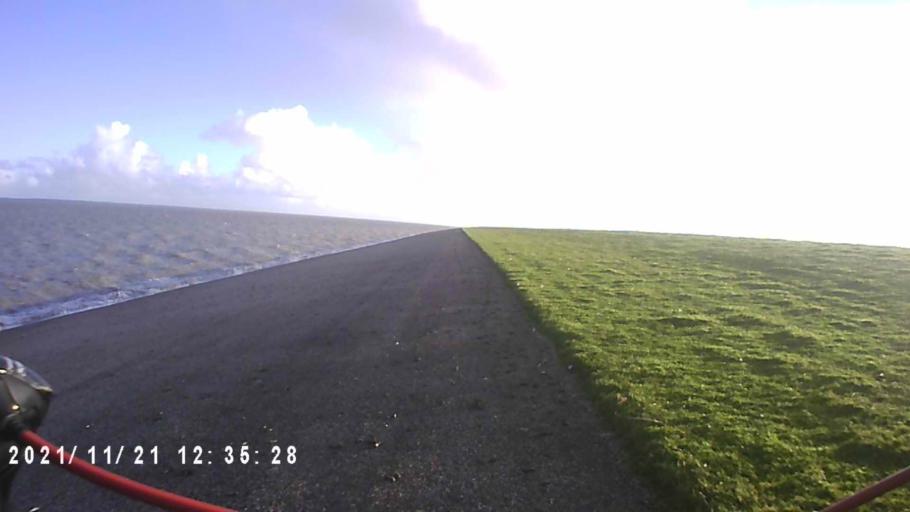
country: NL
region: Friesland
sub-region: Gemeente Dongeradeel
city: Anjum
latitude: 53.4064
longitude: 6.0627
